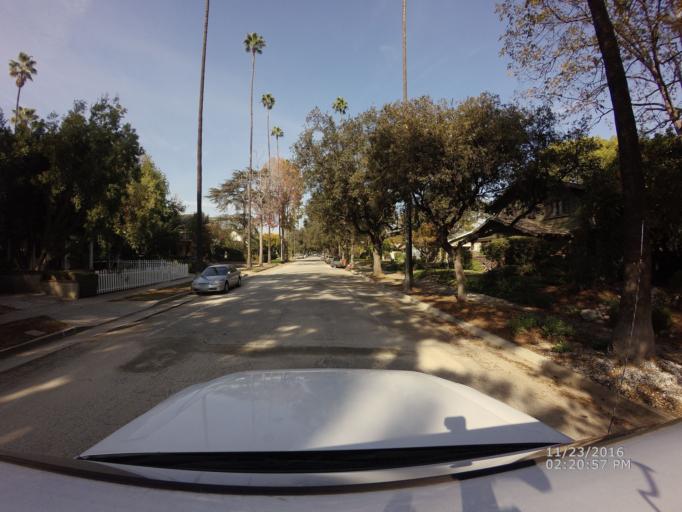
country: US
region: California
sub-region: Los Angeles County
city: Alhambra
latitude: 34.0991
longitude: -118.1424
